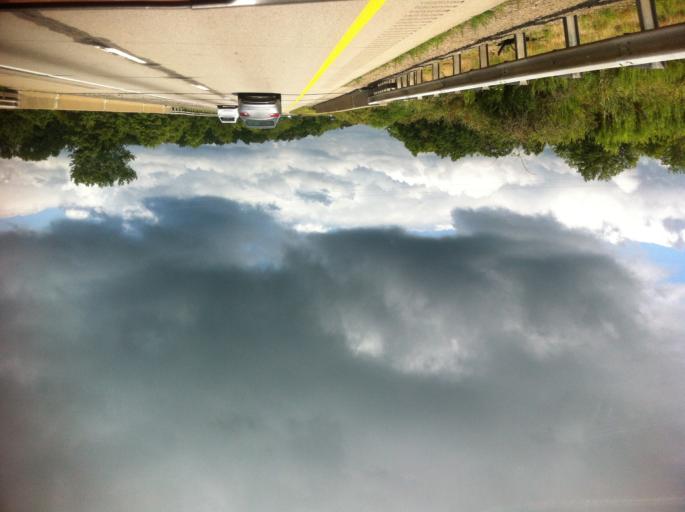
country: US
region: Pennsylvania
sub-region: Lawrence County
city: New Wilmington
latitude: 41.1854
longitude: -80.3633
